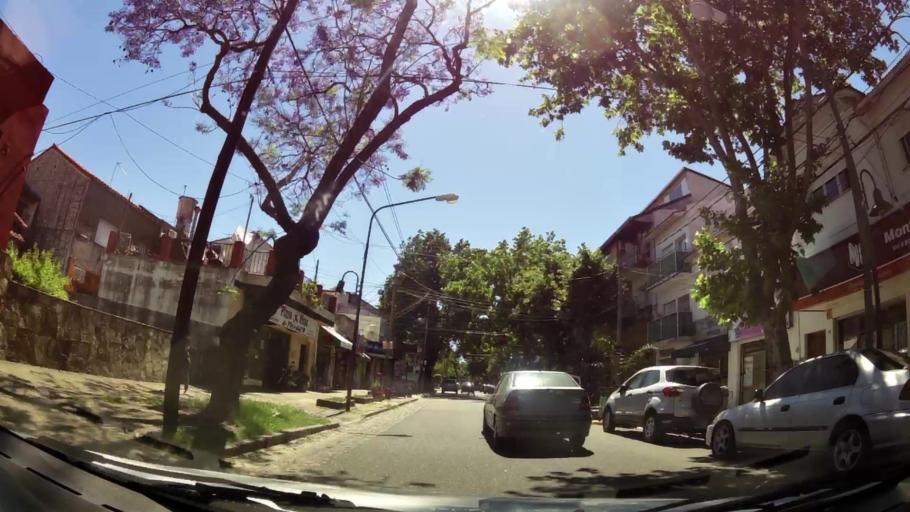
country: AR
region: Buenos Aires
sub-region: Partido de Vicente Lopez
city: Olivos
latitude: -34.5185
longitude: -58.5008
